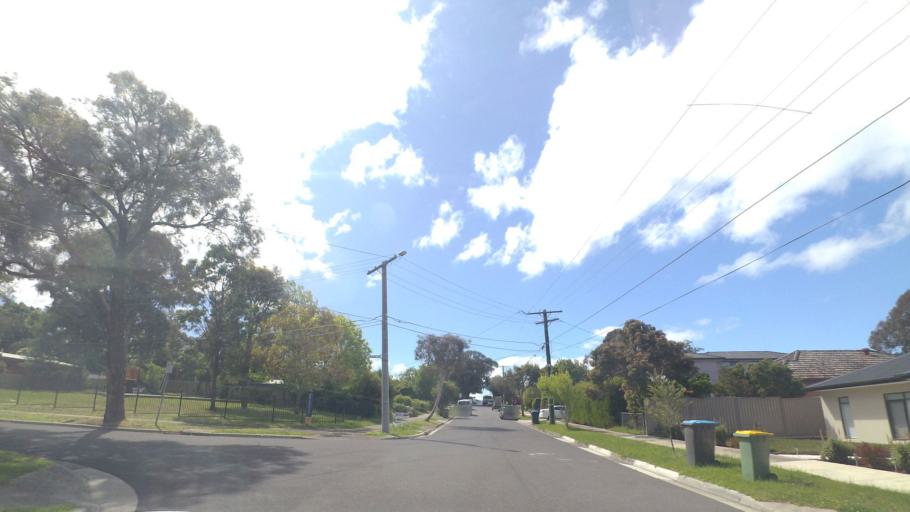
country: AU
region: Victoria
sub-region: Knox
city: Bayswater
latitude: -37.8500
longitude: 145.2665
